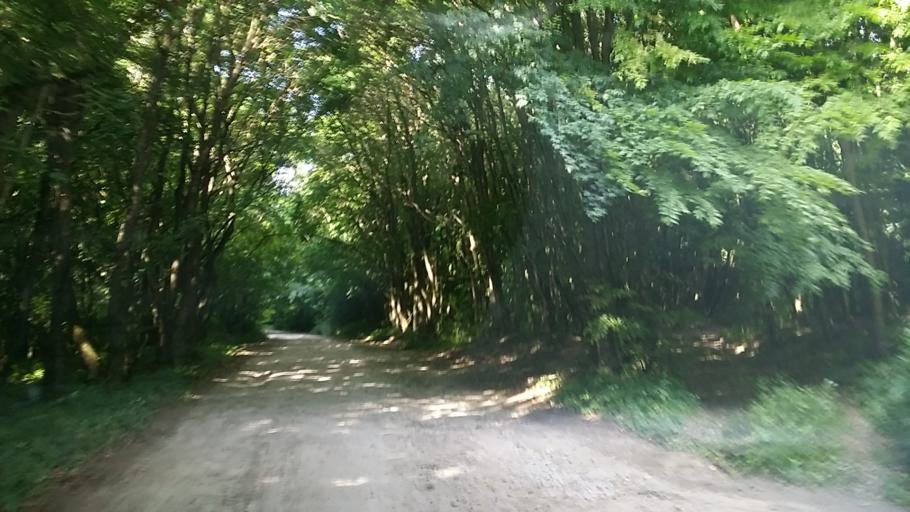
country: HU
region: Komarom-Esztergom
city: Bajna
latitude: 47.6904
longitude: 18.5441
